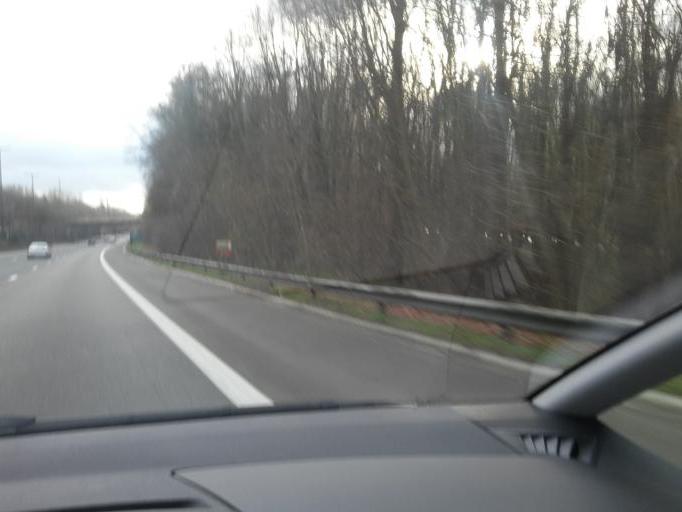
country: BE
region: Flanders
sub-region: Provincie Vlaams-Brabant
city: Hoeilaart
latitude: 50.7878
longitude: 4.4910
